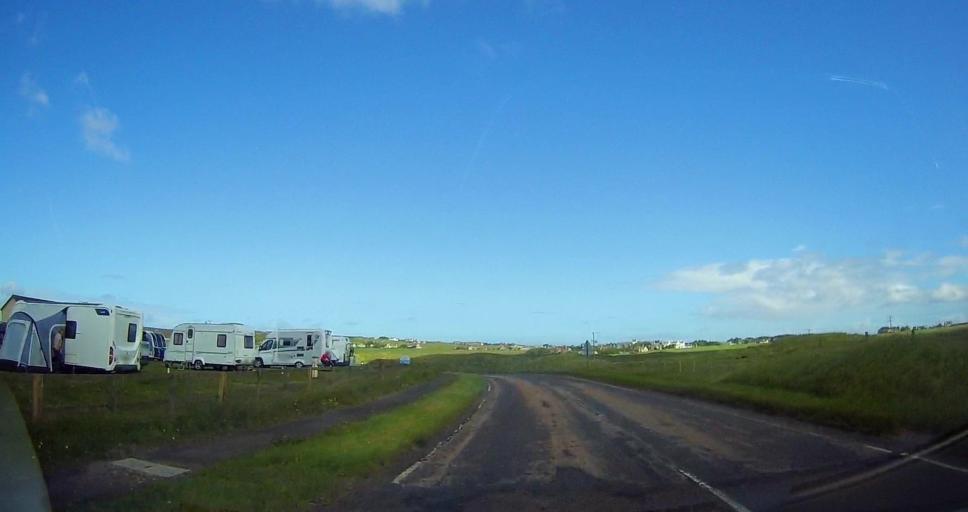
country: GB
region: Scotland
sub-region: Highland
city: Thurso
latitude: 58.6144
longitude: -3.3438
